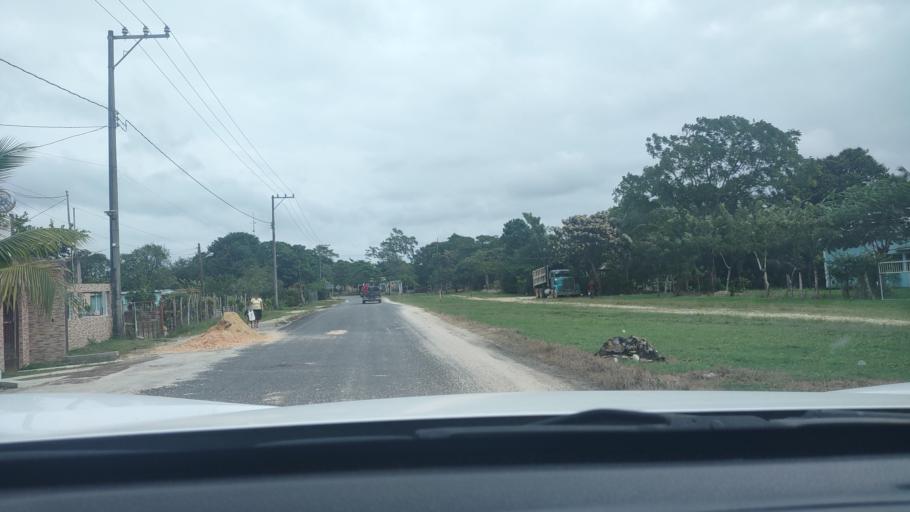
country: MX
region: Veracruz
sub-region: Moloacan
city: Cuichapa
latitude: 17.8994
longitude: -94.2984
